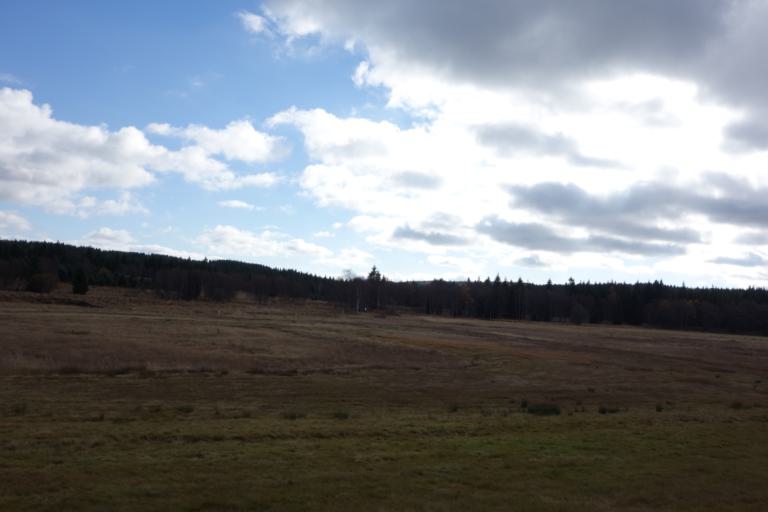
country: DE
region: Saxony
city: Pobershau
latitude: 50.5516
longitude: 13.2270
